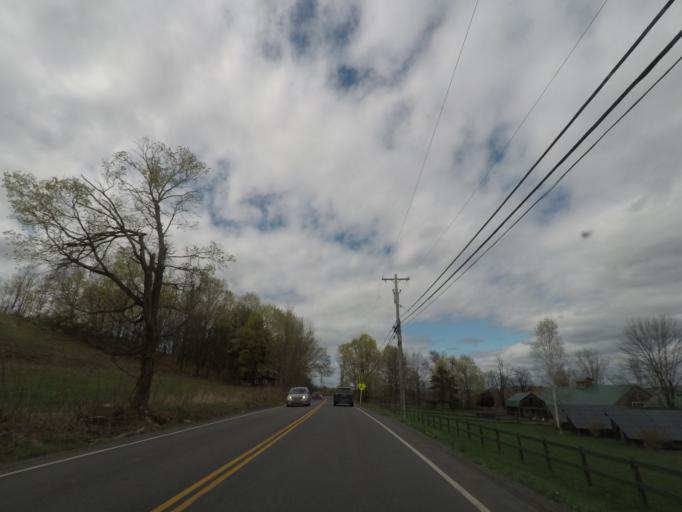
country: US
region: New York
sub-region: Columbia County
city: Valatie
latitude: 42.3817
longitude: -73.6398
